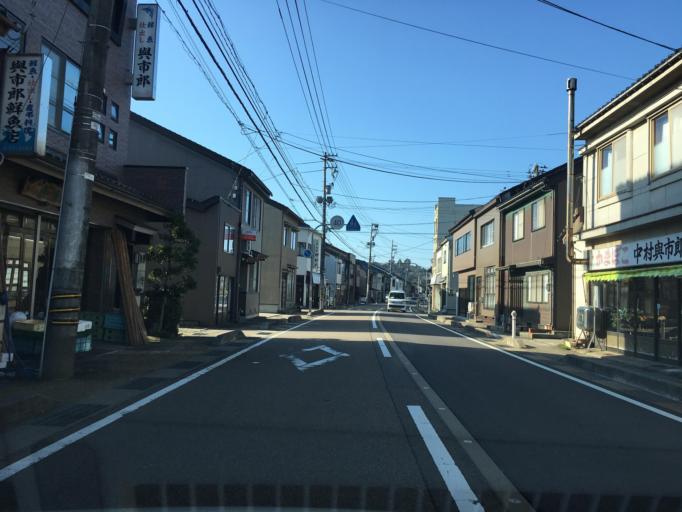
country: JP
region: Toyama
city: Himi
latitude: 36.8675
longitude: 136.9835
